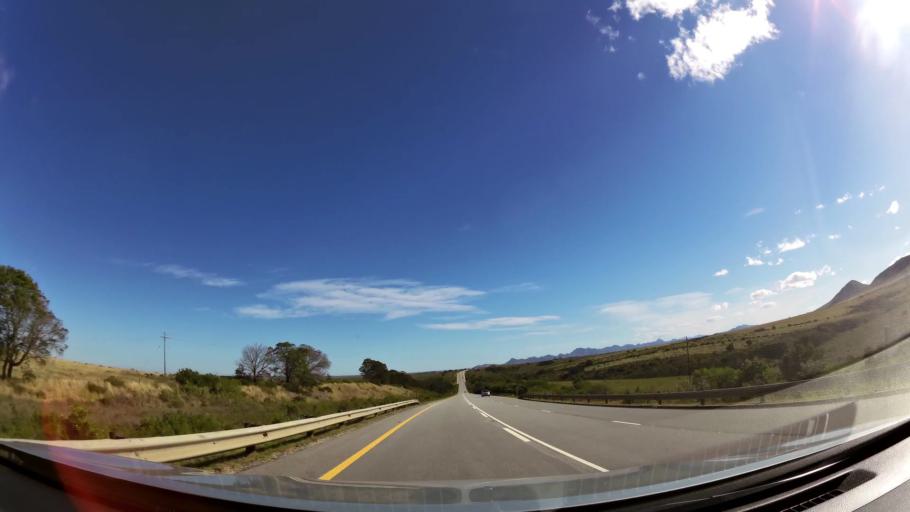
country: ZA
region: Eastern Cape
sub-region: Cacadu District Municipality
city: Kruisfontein
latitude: -34.0054
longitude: 24.6753
